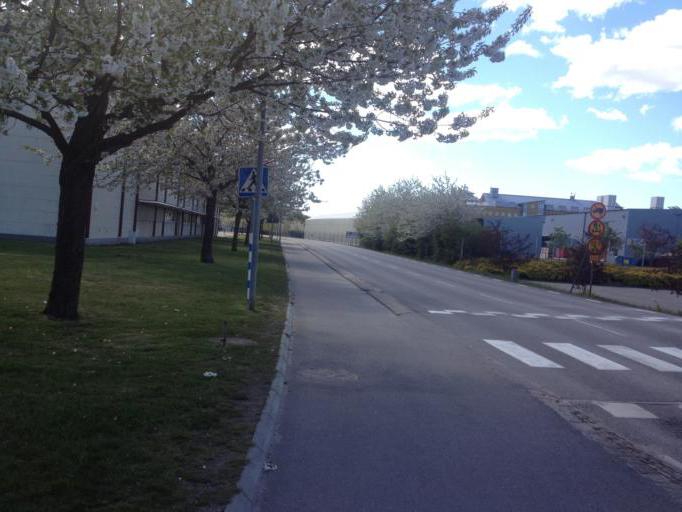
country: SE
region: Blekinge
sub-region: Ronneby Kommun
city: Ronneby
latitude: 56.2025
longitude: 15.2888
